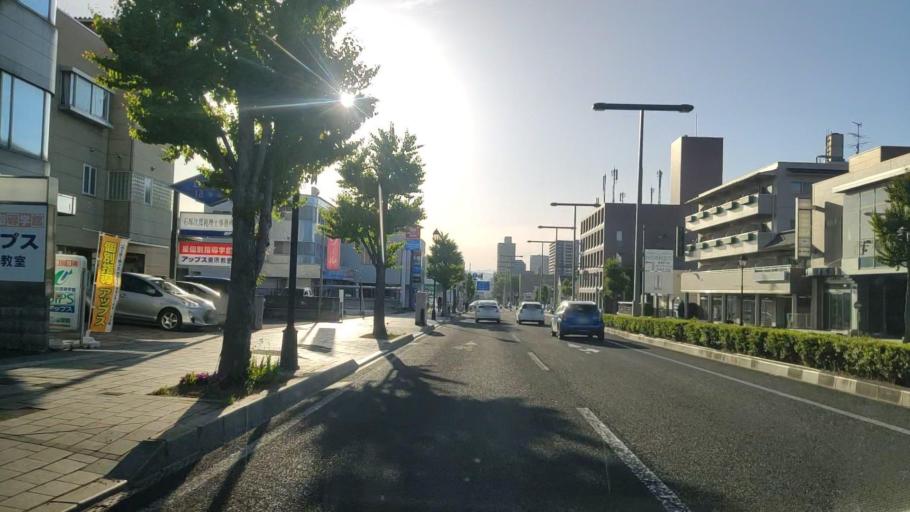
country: JP
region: Yamagata
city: Yamagata-shi
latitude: 38.2430
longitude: 140.3444
